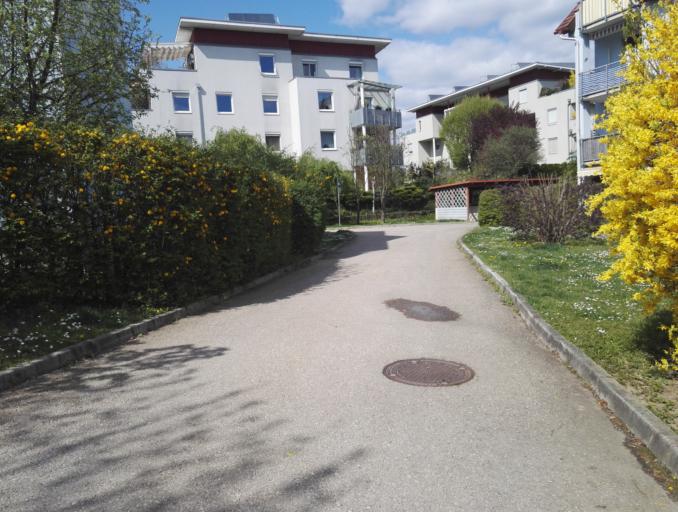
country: AT
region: Styria
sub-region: Graz Stadt
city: Graz
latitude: 47.0494
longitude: 15.4725
